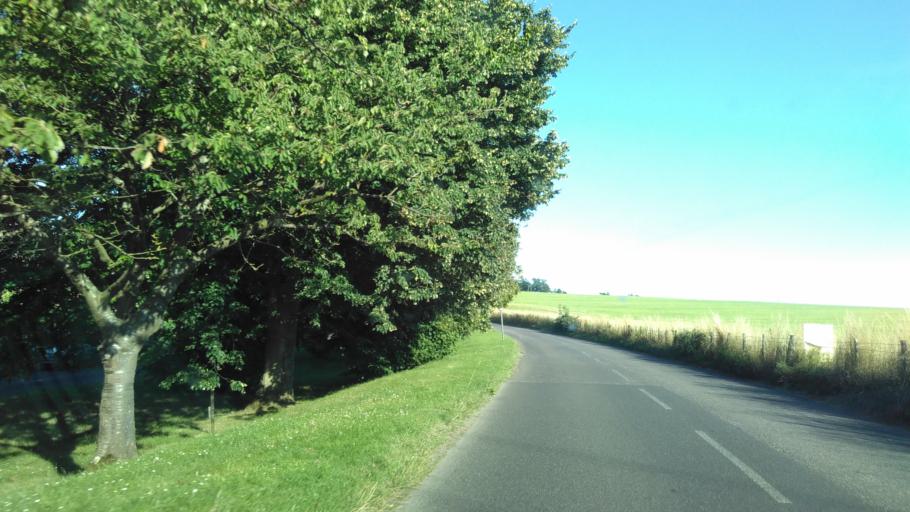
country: GB
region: England
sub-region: Kent
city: Chartham
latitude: 51.2507
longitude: 1.0121
